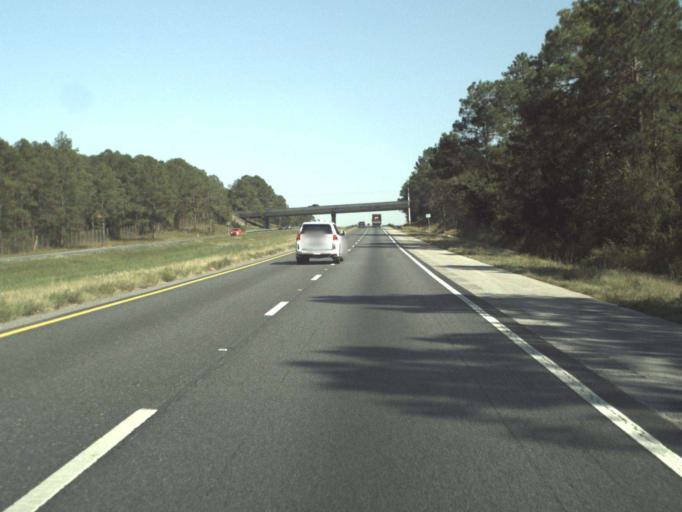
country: US
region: Florida
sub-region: Washington County
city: Chipley
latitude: 30.7524
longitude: -85.5884
